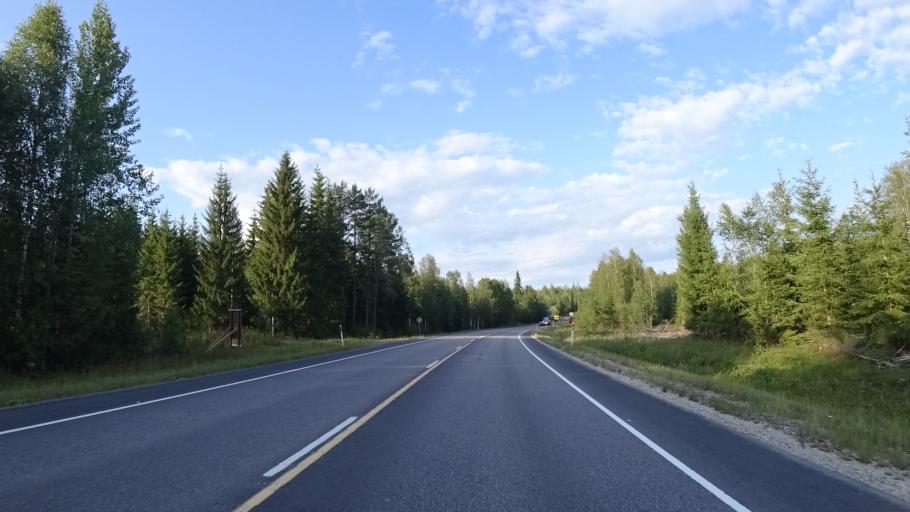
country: FI
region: South Karelia
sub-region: Imatra
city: Ruokolahti
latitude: 61.3170
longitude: 29.0913
